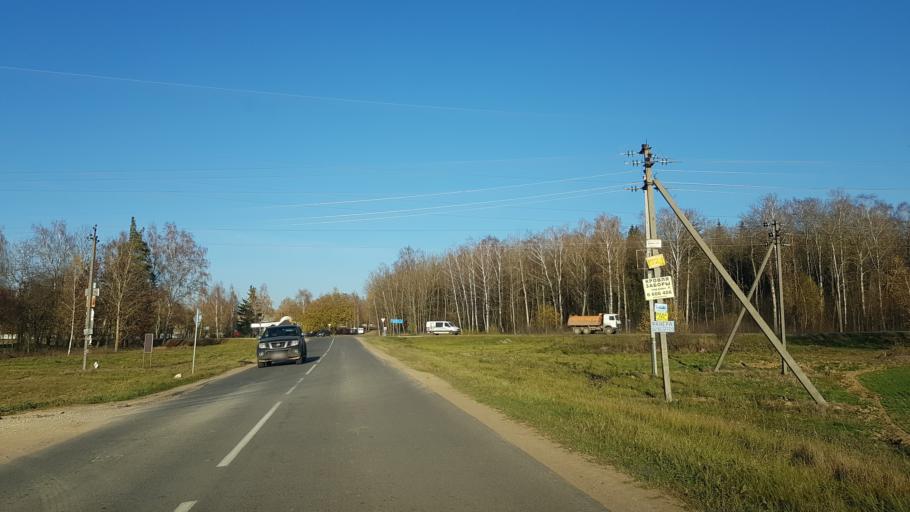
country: BY
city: Fanipol
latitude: 53.7293
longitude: 27.3314
